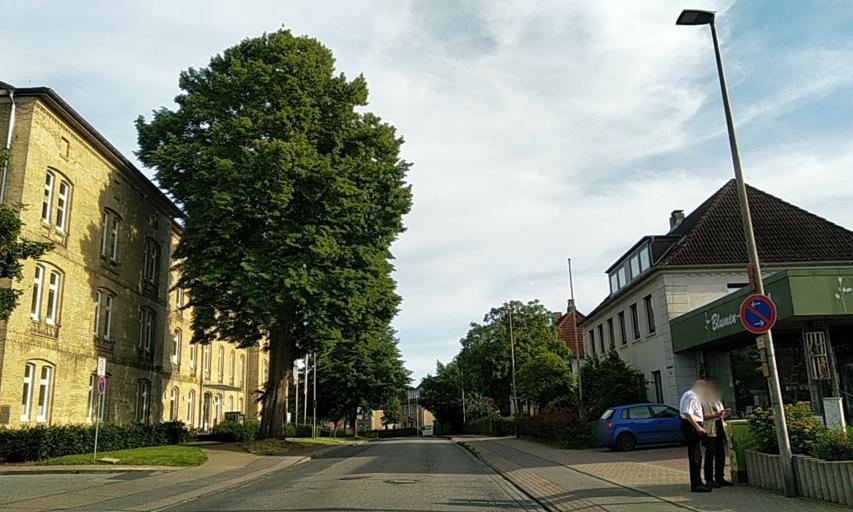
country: DE
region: Schleswig-Holstein
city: Schleswig
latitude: 54.5209
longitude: 9.5569
